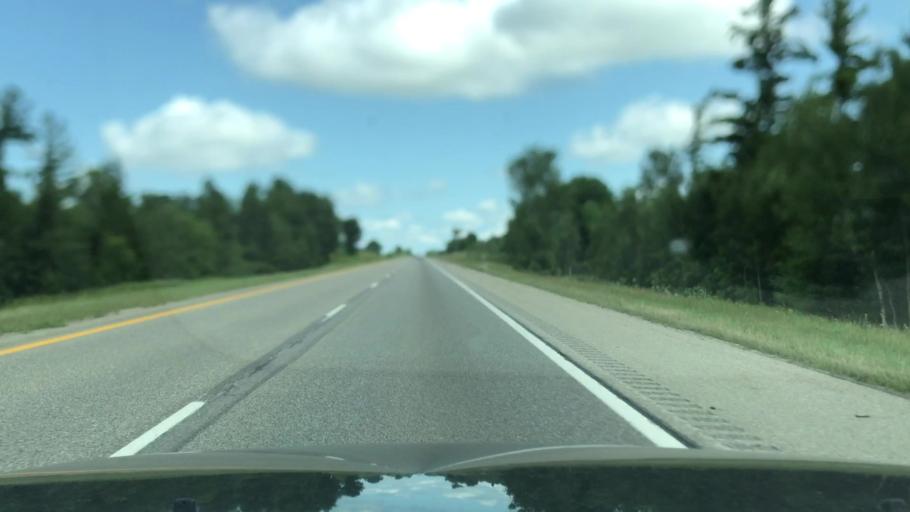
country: US
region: Michigan
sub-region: Mecosta County
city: Big Rapids
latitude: 43.7044
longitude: -85.5282
